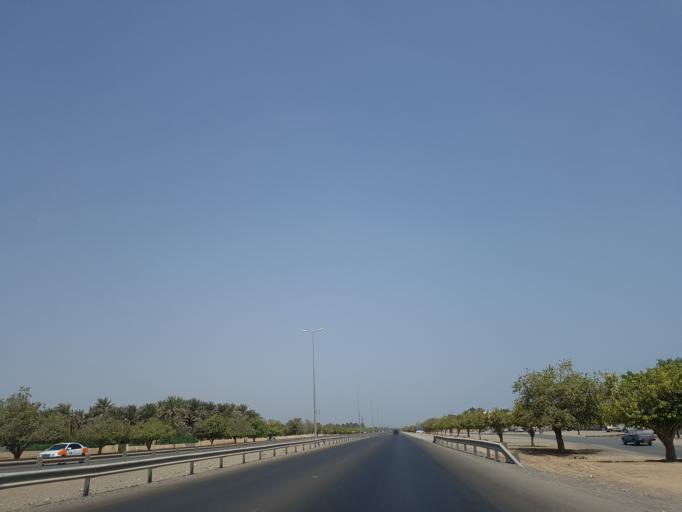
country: OM
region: Al Batinah
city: Saham
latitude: 24.1648
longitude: 56.8627
